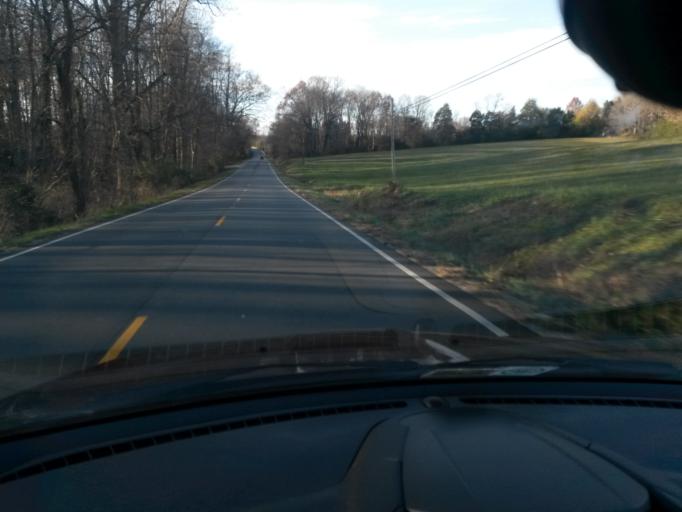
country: US
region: Virginia
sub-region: Amherst County
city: Amherst
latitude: 37.6001
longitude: -79.0625
